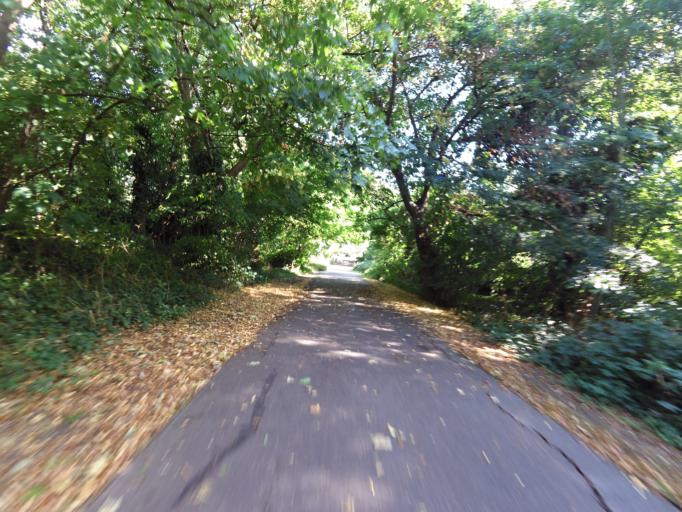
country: GB
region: England
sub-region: Greater London
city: Wood Green
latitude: 51.6230
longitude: -0.1367
